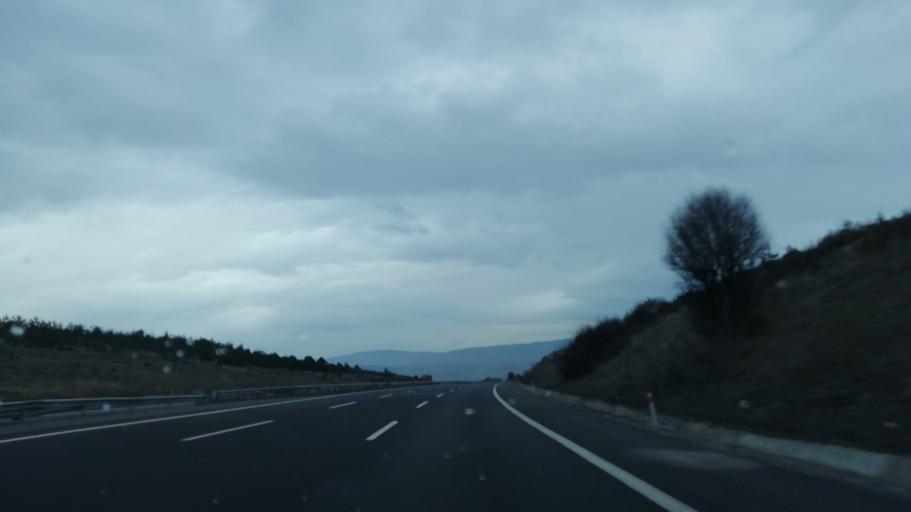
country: TR
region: Bolu
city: Yenicaga
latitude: 40.7583
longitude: 32.0642
